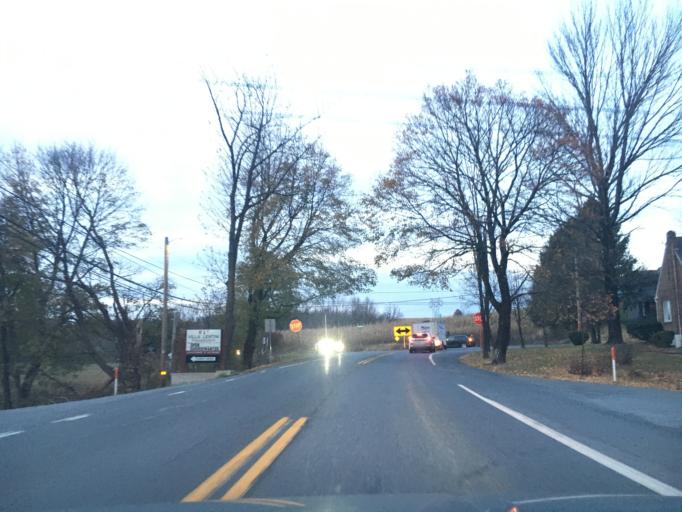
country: US
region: Pennsylvania
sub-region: Lehigh County
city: Schnecksville
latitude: 40.6782
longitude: -75.5709
